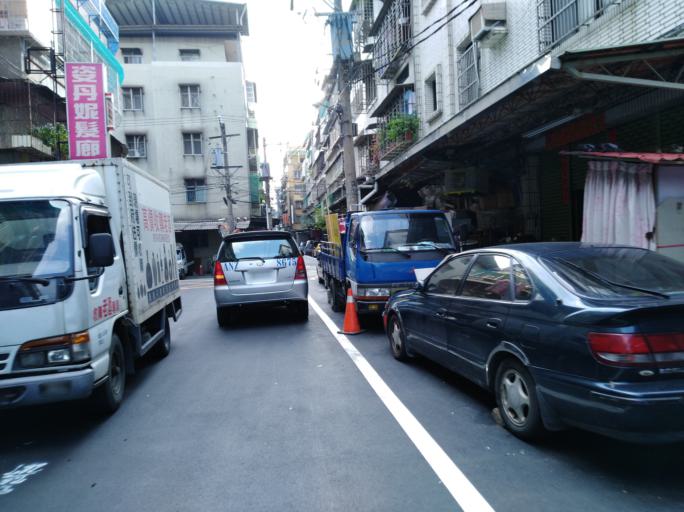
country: TW
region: Taipei
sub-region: Taipei
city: Banqiao
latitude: 25.0403
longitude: 121.4255
